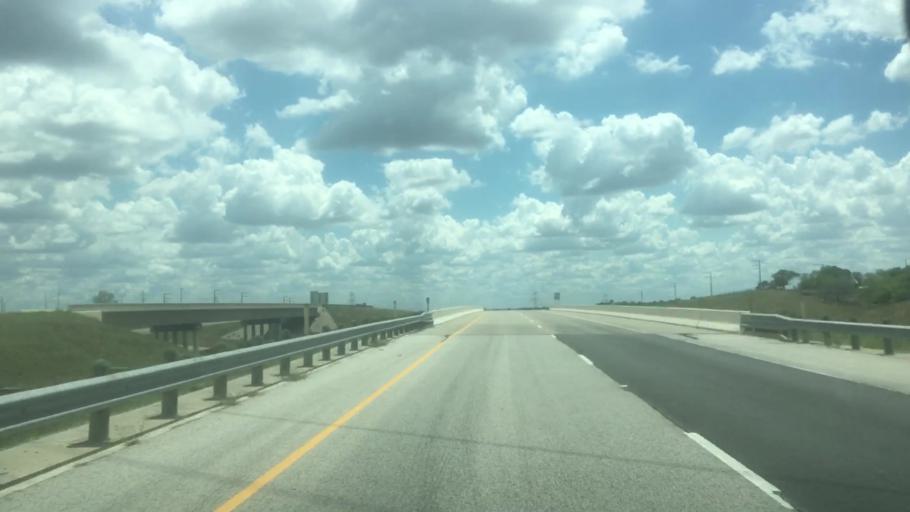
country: US
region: Texas
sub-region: Caldwell County
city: Uhland
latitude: 30.0062
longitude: -97.6875
